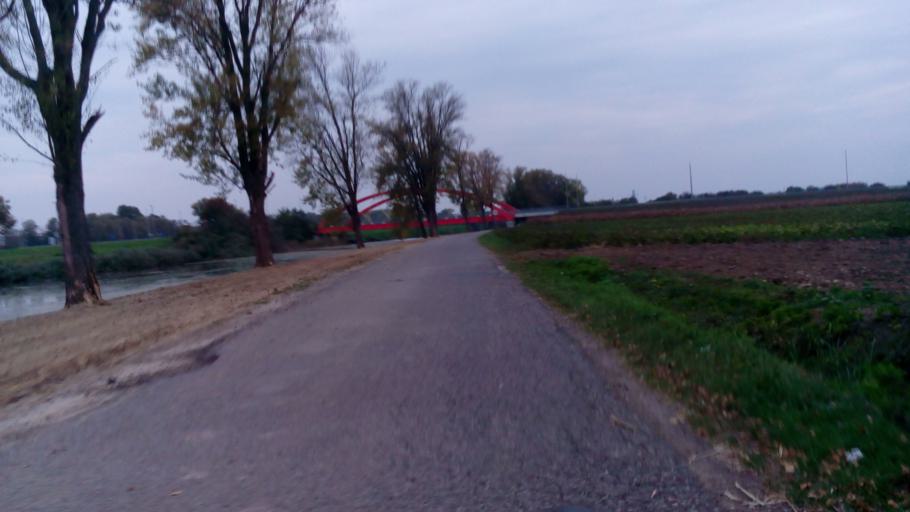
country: HR
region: Vukovarsko-Srijemska
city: Vinkovci
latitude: 45.2646
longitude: 18.8112
